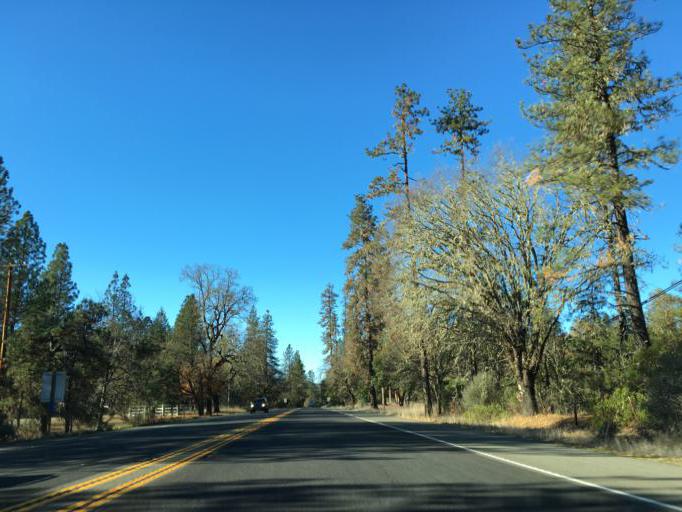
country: US
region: California
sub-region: Mendocino County
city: Laytonville
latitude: 39.7310
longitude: -123.5091
